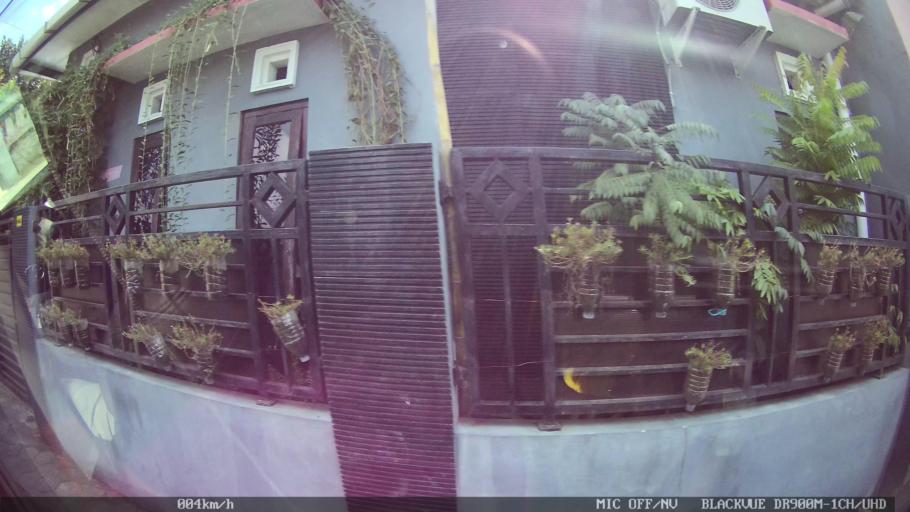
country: ID
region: Daerah Istimewa Yogyakarta
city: Depok
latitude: -7.8081
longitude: 110.4069
